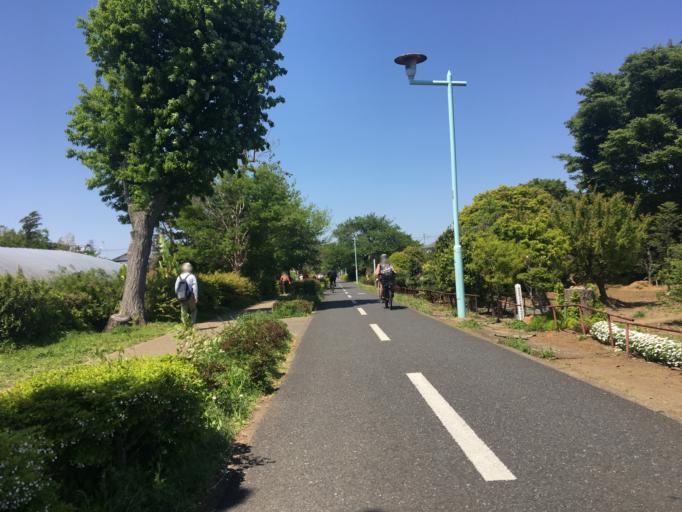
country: JP
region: Tokyo
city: Nishi-Tokyo-shi
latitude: 35.7184
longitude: 139.5294
